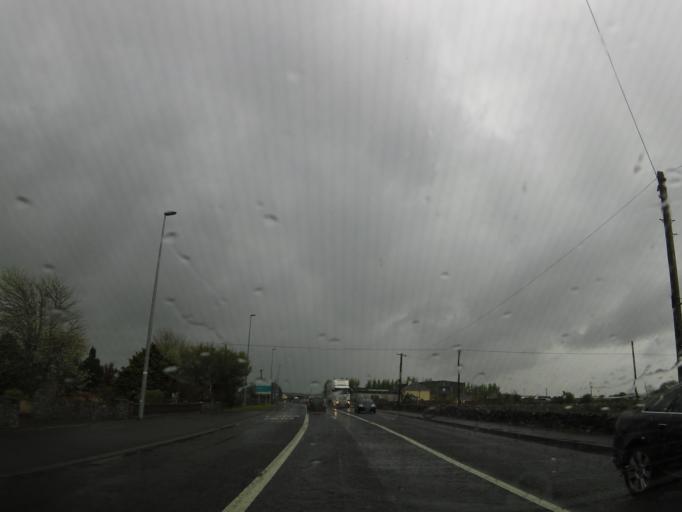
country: IE
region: Connaught
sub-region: County Galway
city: Claregalway
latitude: 53.3515
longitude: -8.9372
